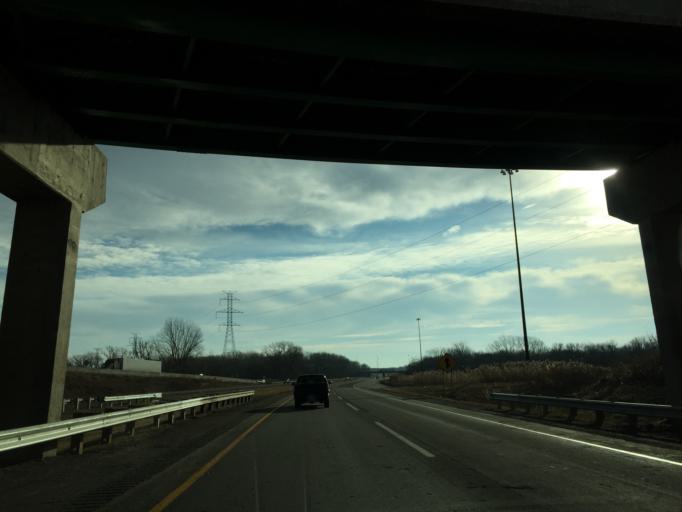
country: US
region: Indiana
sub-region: Lake County
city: Lake Station
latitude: 41.5927
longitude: -87.2330
